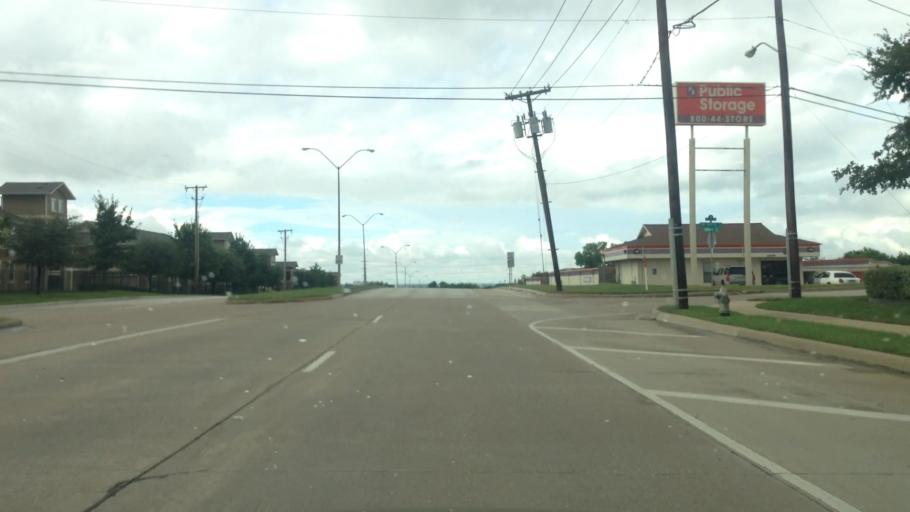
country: US
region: Texas
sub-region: Tarrant County
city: Benbrook
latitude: 32.6462
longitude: -97.4095
